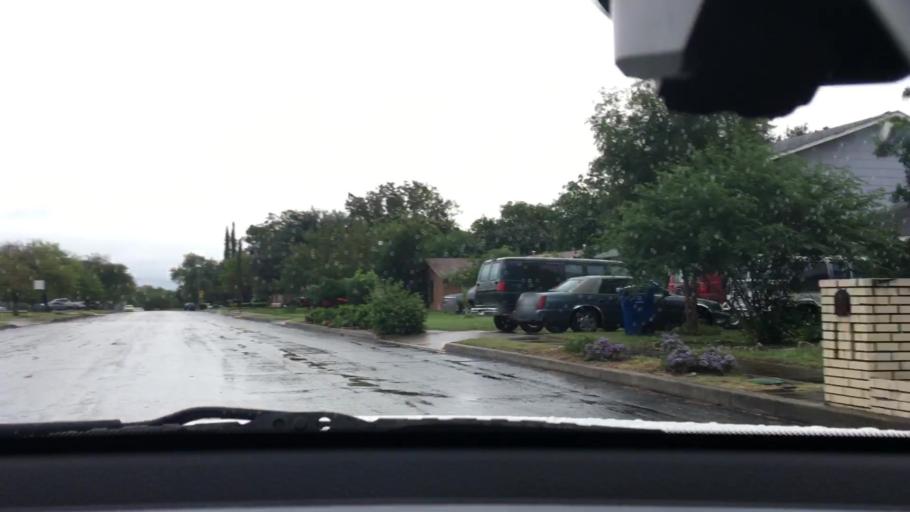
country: US
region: Texas
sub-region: Bexar County
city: Windcrest
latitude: 29.5045
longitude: -98.3826
